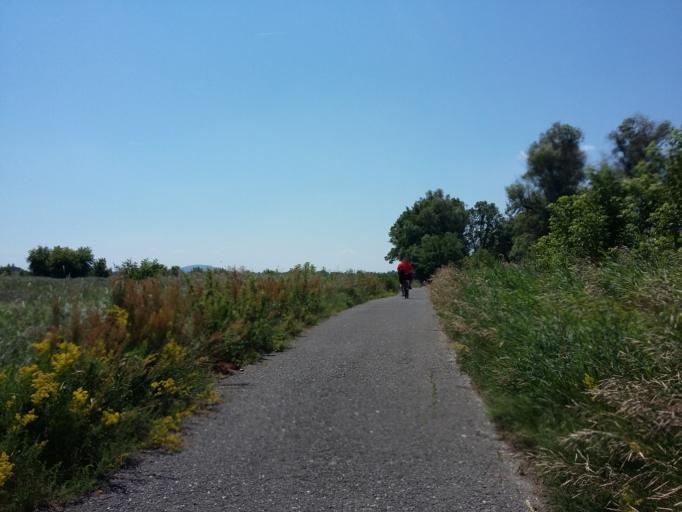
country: AT
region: Lower Austria
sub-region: Politischer Bezirk Ganserndorf
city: Marchegg
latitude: 48.2620
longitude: 16.9575
